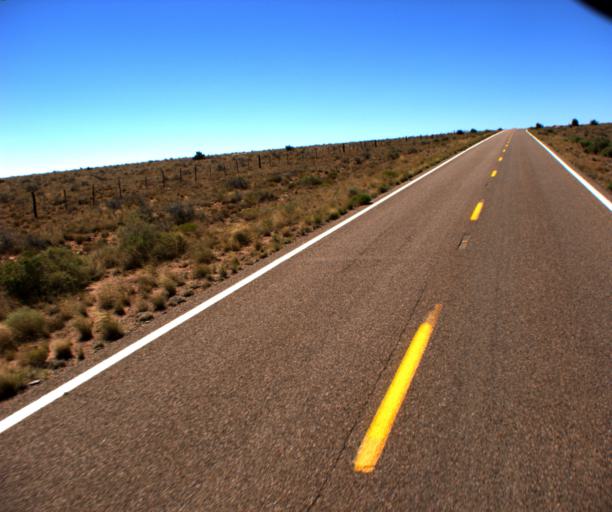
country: US
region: Arizona
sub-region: Navajo County
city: Winslow
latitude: 34.9328
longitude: -110.6395
